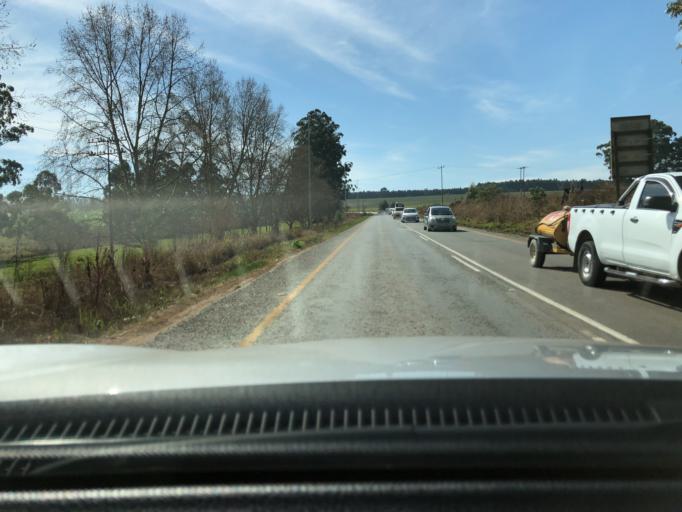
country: ZA
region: KwaZulu-Natal
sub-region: Sisonke District Municipality
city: Ixopo
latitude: -30.1430
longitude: 30.0735
